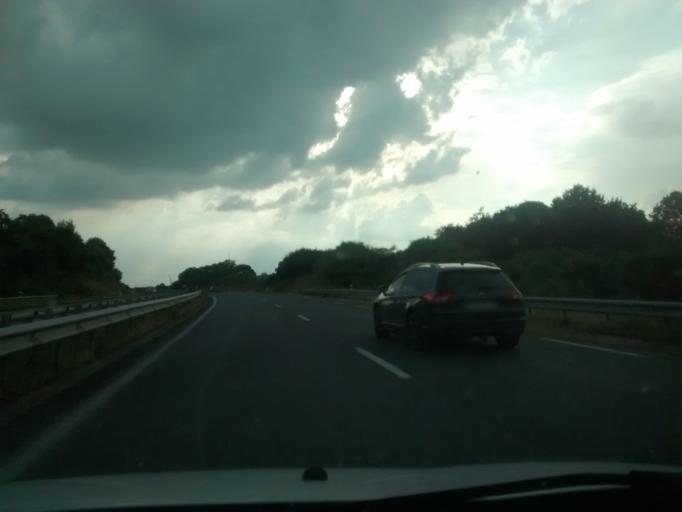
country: FR
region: Brittany
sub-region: Departement des Cotes-d'Armor
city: Begard
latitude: 48.6180
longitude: -3.2951
